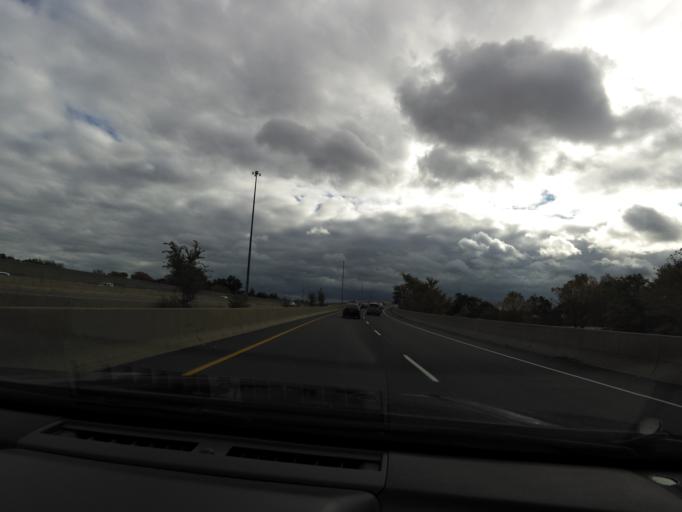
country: CA
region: Ontario
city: Kitchener
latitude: 43.4409
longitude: -80.4562
